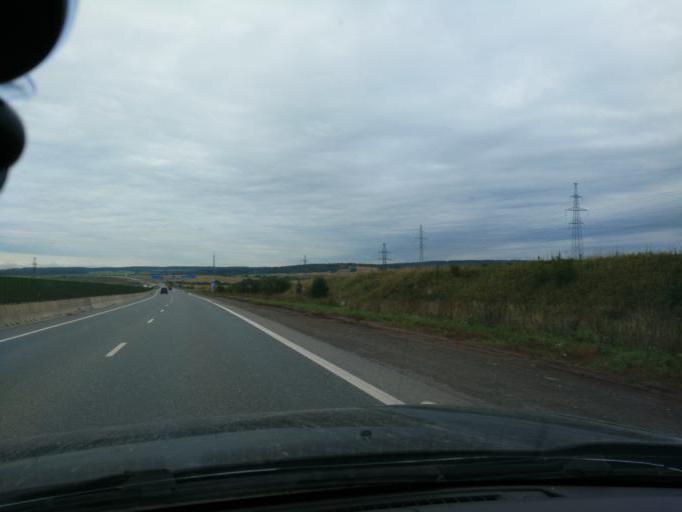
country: RU
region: Perm
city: Ferma
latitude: 57.9301
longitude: 56.3231
